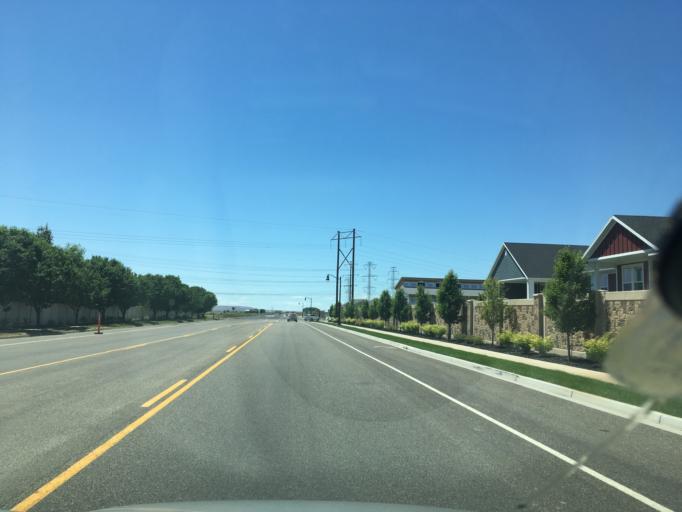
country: US
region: Utah
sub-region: Davis County
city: Layton
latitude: 41.0493
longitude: -111.9956
